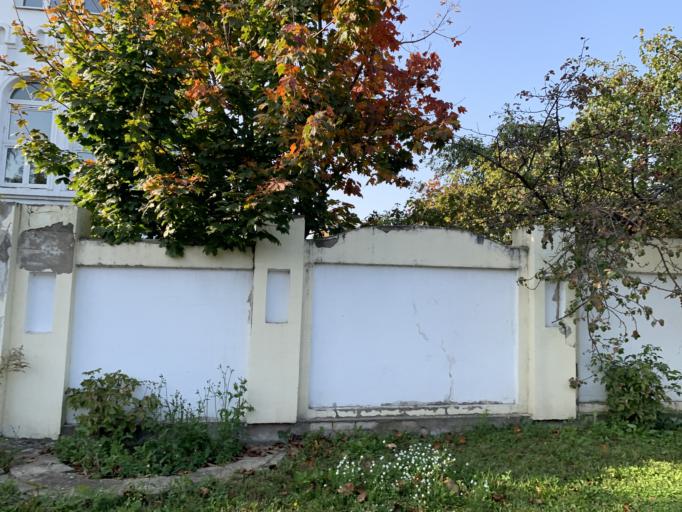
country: RU
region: Moskovskaya
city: Lesnyye Polyany
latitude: 55.9657
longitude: 37.8447
